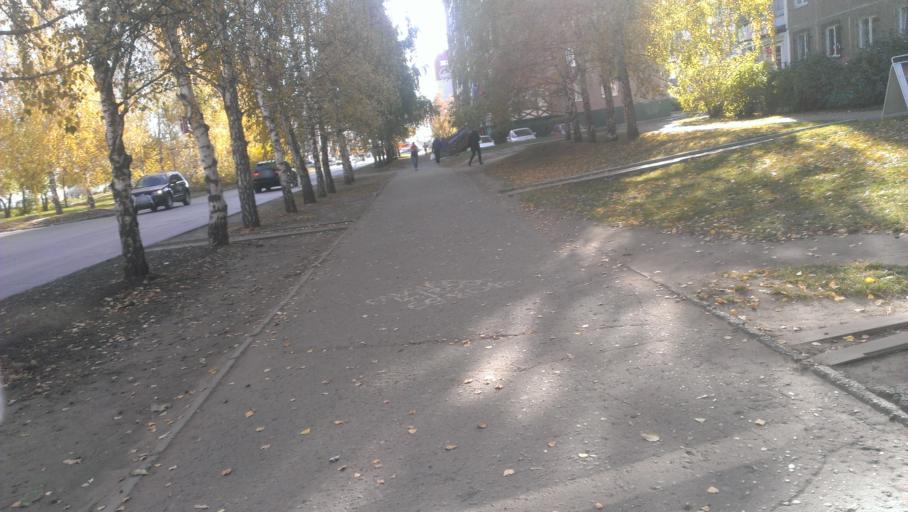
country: RU
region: Altai Krai
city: Novosilikatnyy
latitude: 53.3320
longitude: 83.6760
